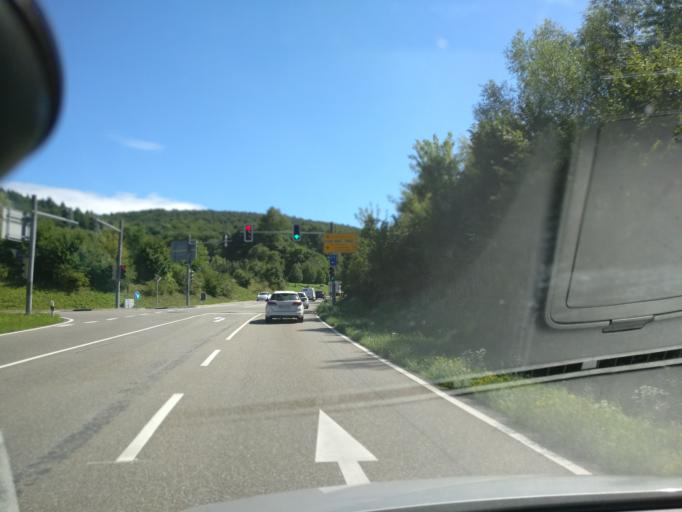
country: DE
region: Baden-Wuerttemberg
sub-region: Karlsruhe Region
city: Ettlingen
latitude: 48.9703
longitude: 8.4462
